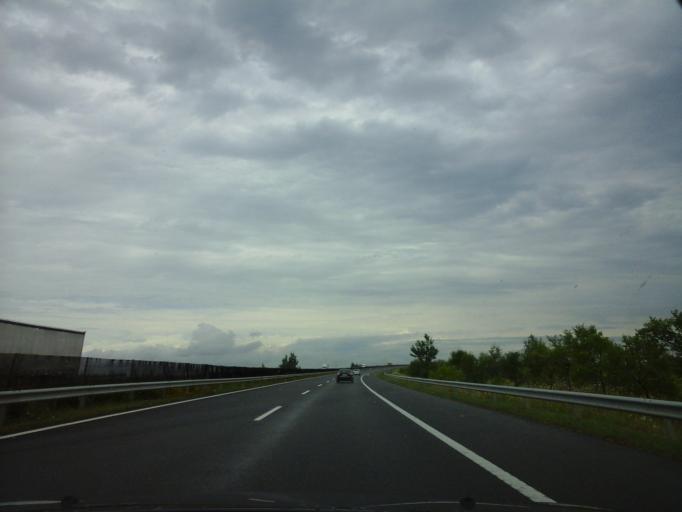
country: HU
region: Hajdu-Bihar
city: Polgar
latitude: 47.8153
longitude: 21.1555
